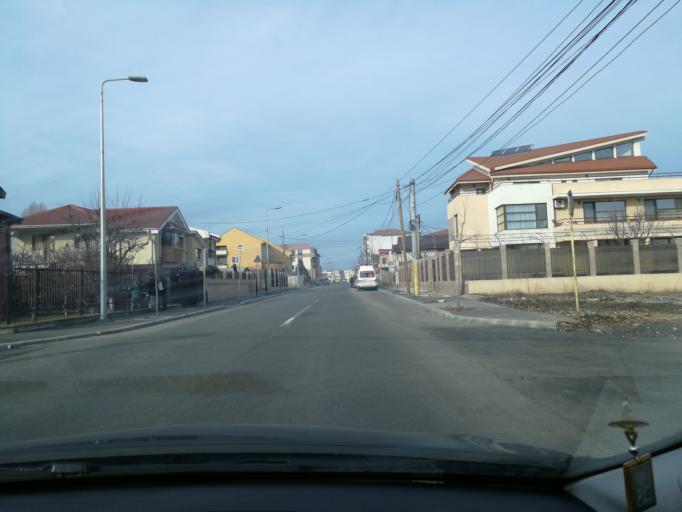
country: RO
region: Constanta
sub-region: Municipiul Constanta
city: Constanta
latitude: 44.1812
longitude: 28.6118
